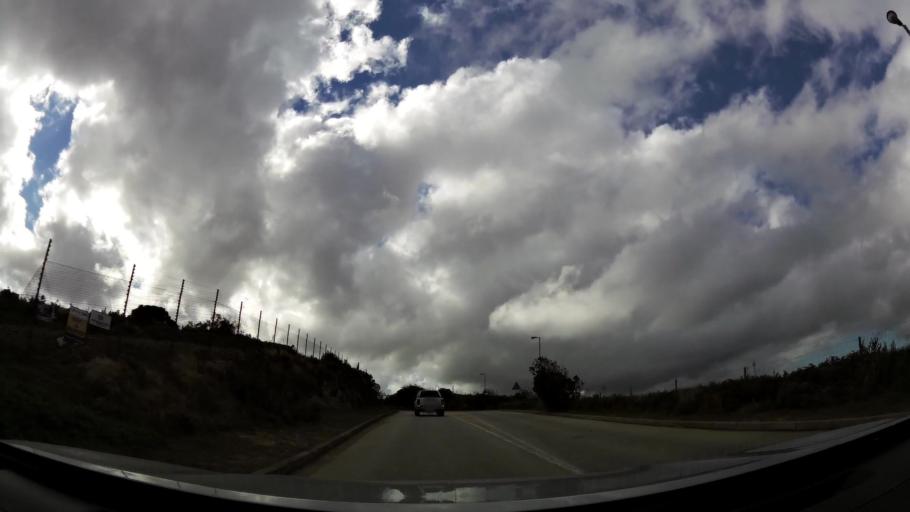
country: ZA
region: Western Cape
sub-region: Eden District Municipality
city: Knysna
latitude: -34.0728
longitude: 23.0866
